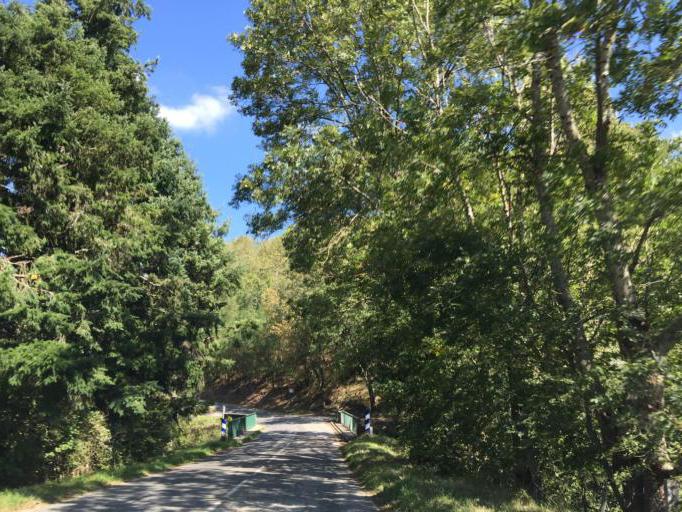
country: FR
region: Rhone-Alpes
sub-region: Departement de la Loire
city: Saint-Paul-en-Jarez
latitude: 45.4336
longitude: 4.5759
